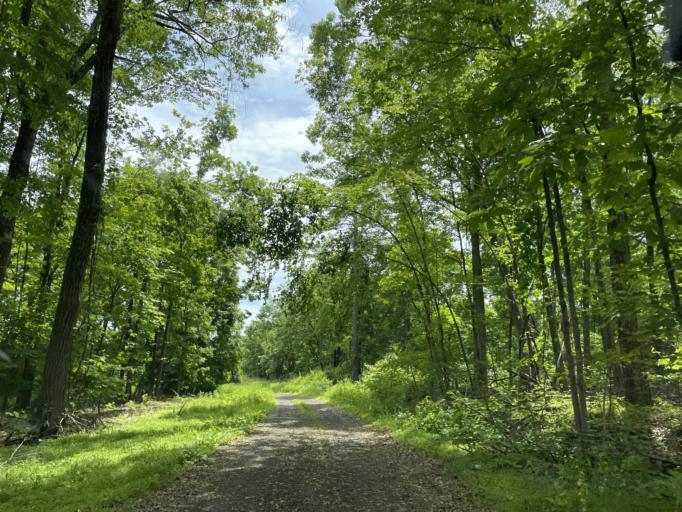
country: US
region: New York
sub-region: Ulster County
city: Lincoln Park
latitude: 41.9674
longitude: -74.0323
